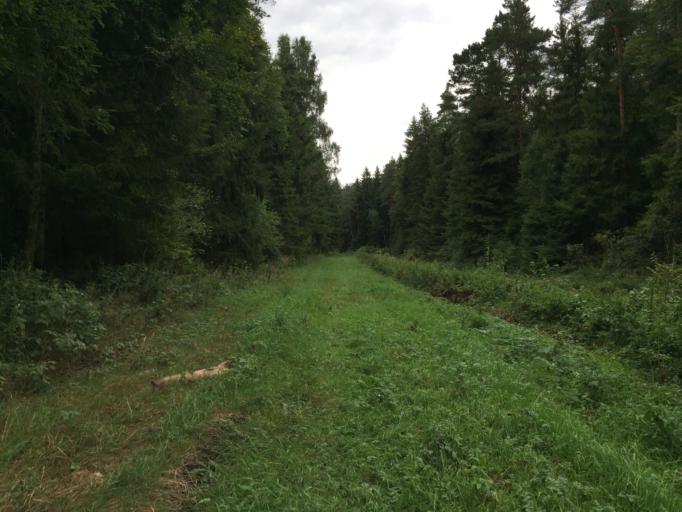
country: LV
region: Jaunpils
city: Jaunpils
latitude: 56.7286
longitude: 23.0881
